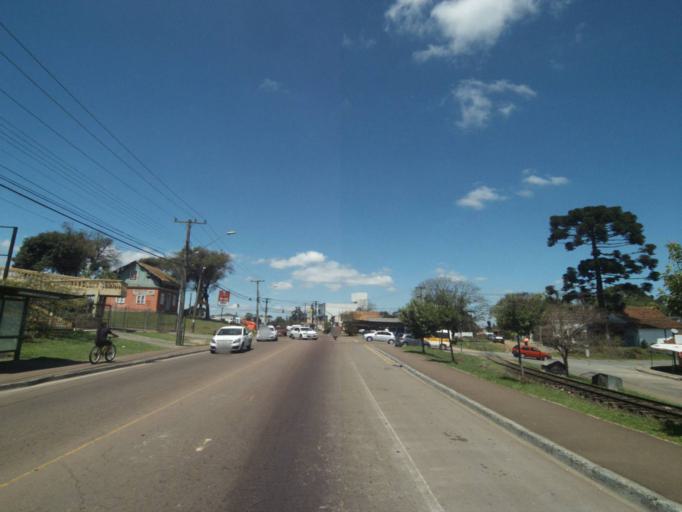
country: BR
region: Parana
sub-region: Curitiba
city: Curitiba
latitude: -25.3763
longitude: -49.2627
